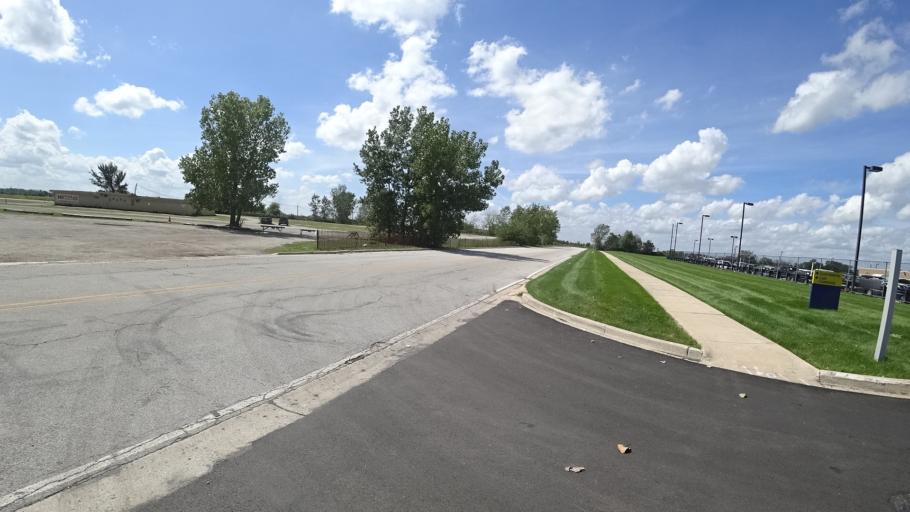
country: US
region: Illinois
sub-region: Cook County
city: Tinley Park
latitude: 41.5472
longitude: -87.7852
